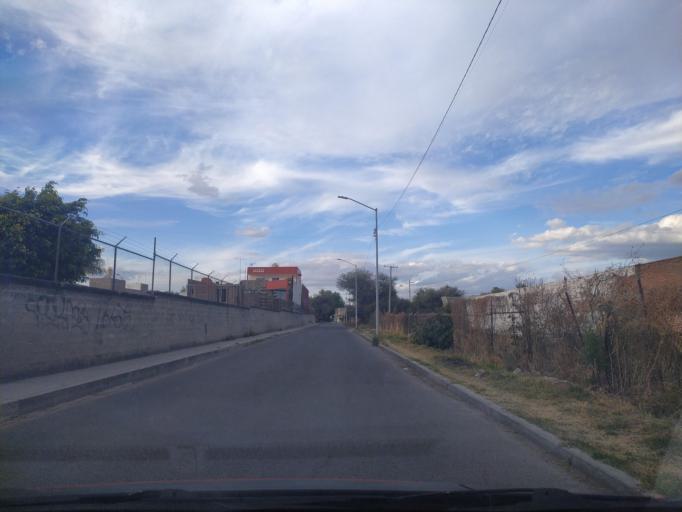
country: LA
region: Oudomxai
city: Muang La
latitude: 21.0322
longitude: 101.8837
